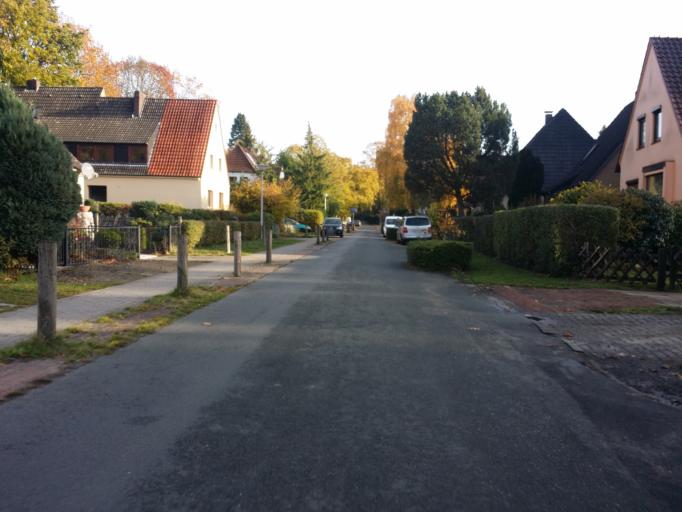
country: DE
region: Lower Saxony
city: Stuhr
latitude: 53.0403
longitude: 8.7227
